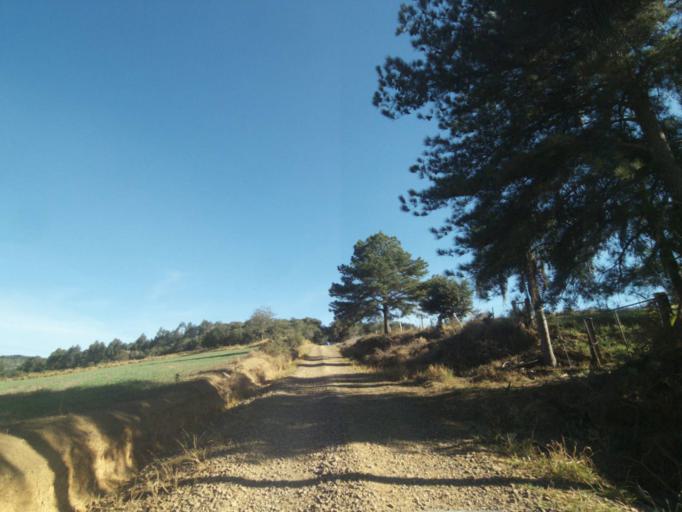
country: BR
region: Parana
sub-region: Tibagi
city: Tibagi
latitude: -24.5521
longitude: -50.5204
